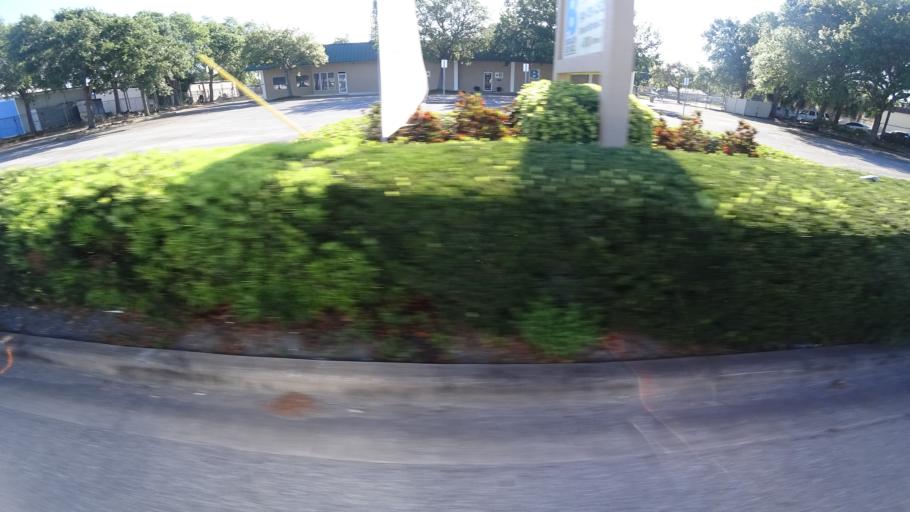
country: US
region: Florida
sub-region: Manatee County
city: South Bradenton
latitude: 27.4764
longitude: -82.5877
